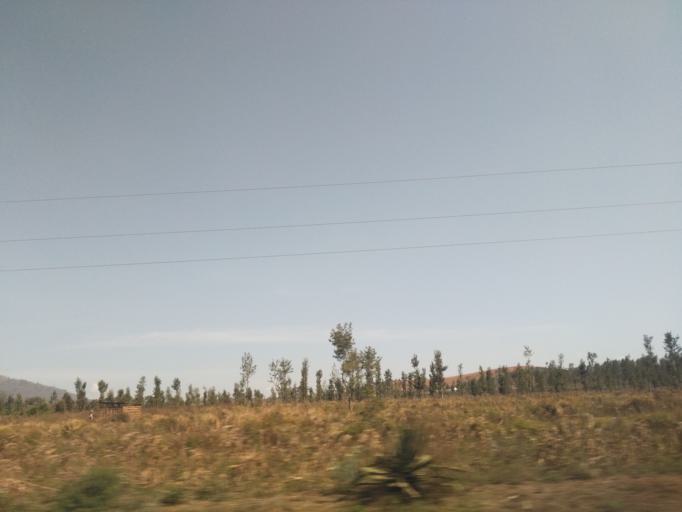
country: TZ
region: Arusha
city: Arusha
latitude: -3.2149
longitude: 36.6122
